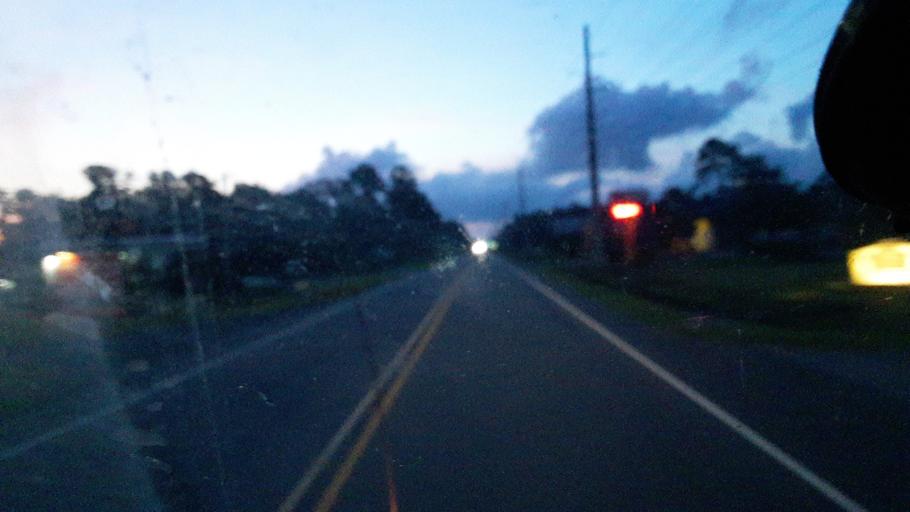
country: US
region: North Carolina
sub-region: Brunswick County
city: Oak Island
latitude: 33.9908
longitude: -78.2090
